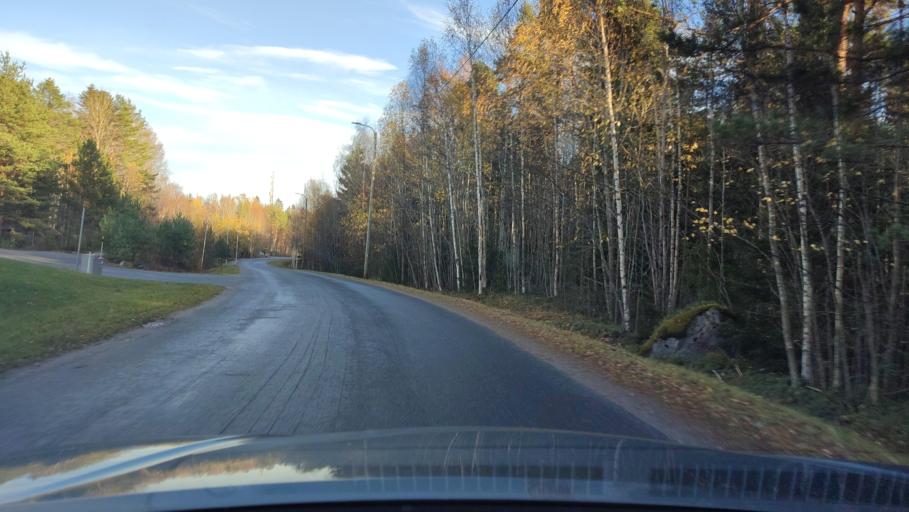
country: FI
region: Ostrobothnia
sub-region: Vaasa
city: Teeriniemi
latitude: 63.0664
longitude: 21.6935
